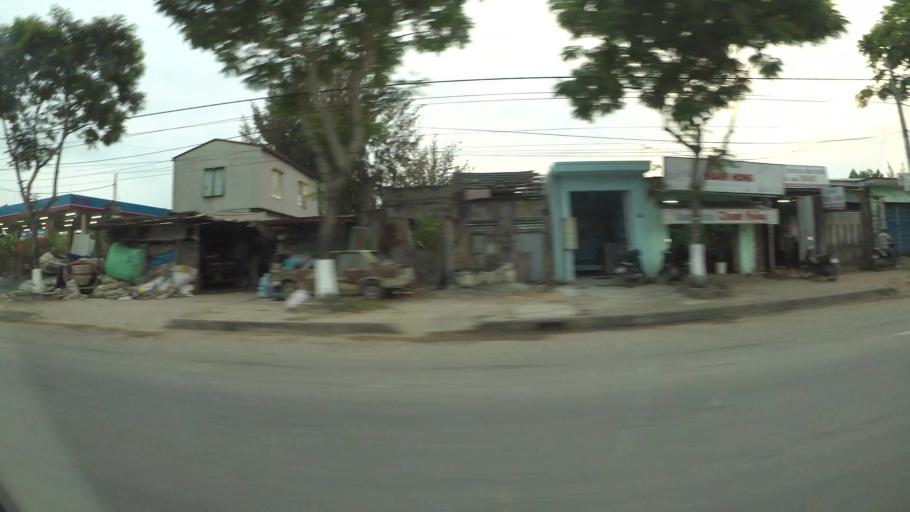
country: VN
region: Da Nang
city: Lien Chieu
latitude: 16.0928
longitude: 108.1407
